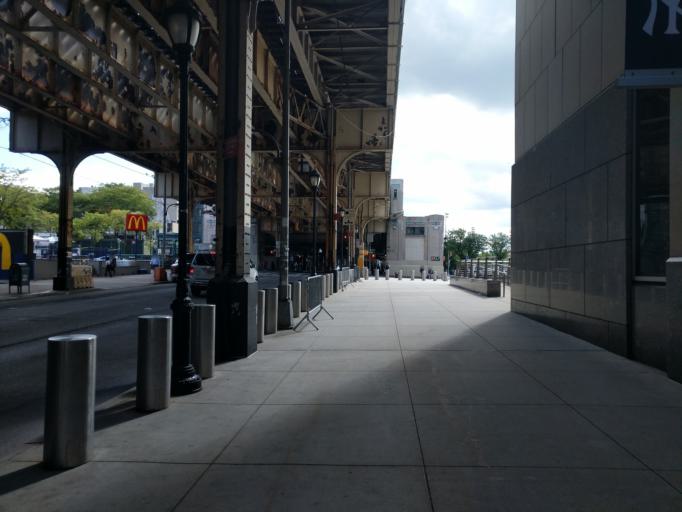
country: US
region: New York
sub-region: New York County
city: Inwood
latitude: 40.8286
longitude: -73.9258
